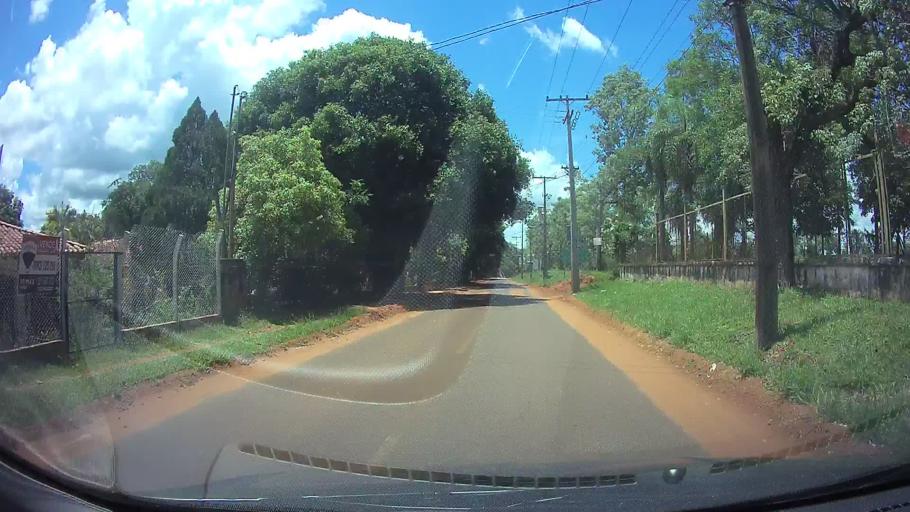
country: PY
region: Central
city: Itaugua
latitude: -25.3765
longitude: -57.3662
